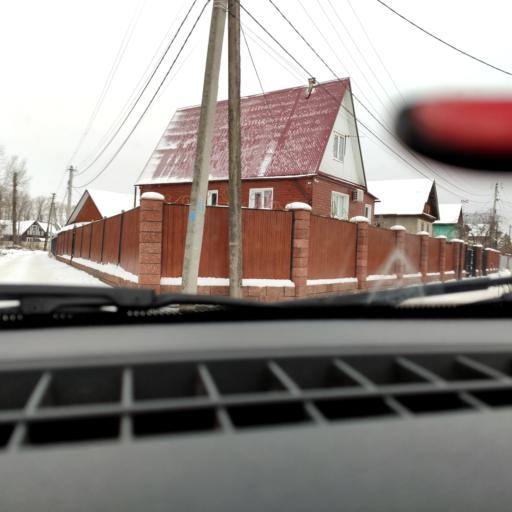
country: RU
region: Bashkortostan
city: Ufa
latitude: 54.6316
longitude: 55.8884
